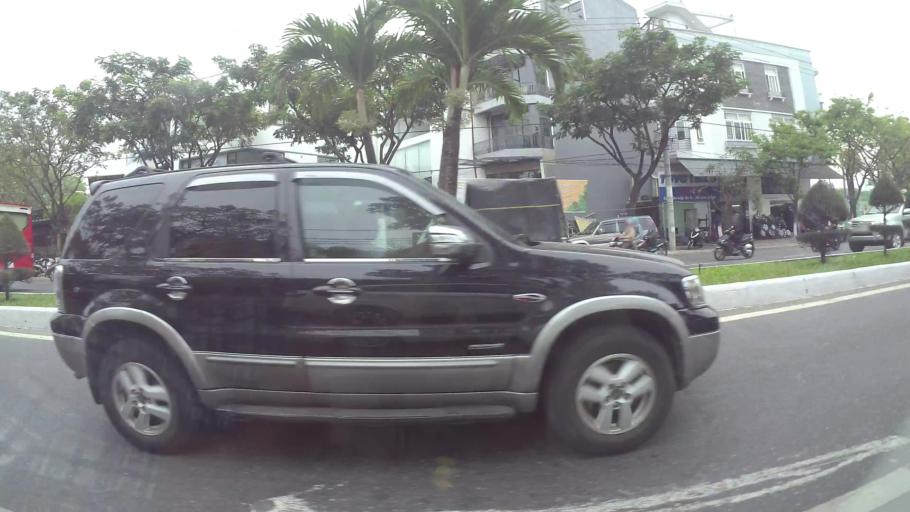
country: VN
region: Da Nang
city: Da Nang
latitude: 16.0478
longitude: 108.2094
